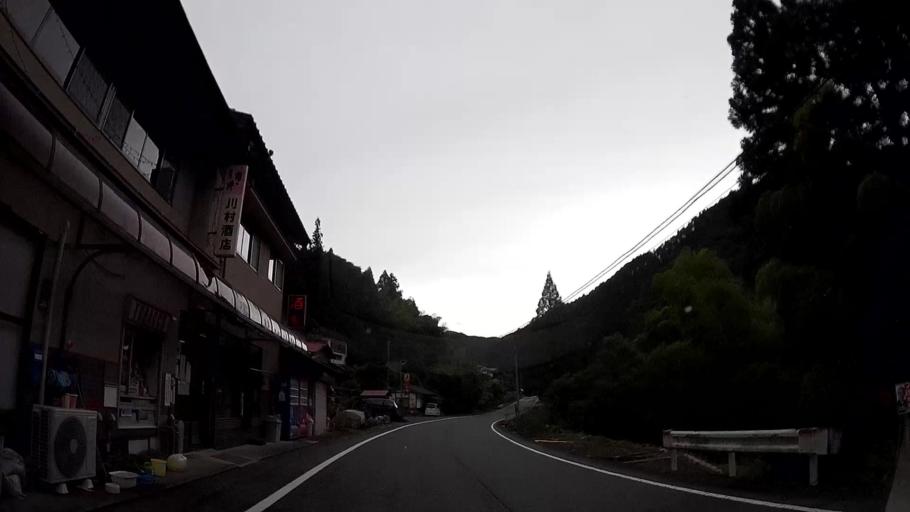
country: JP
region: Kumamoto
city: Kikuchi
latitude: 33.0838
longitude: 130.9456
